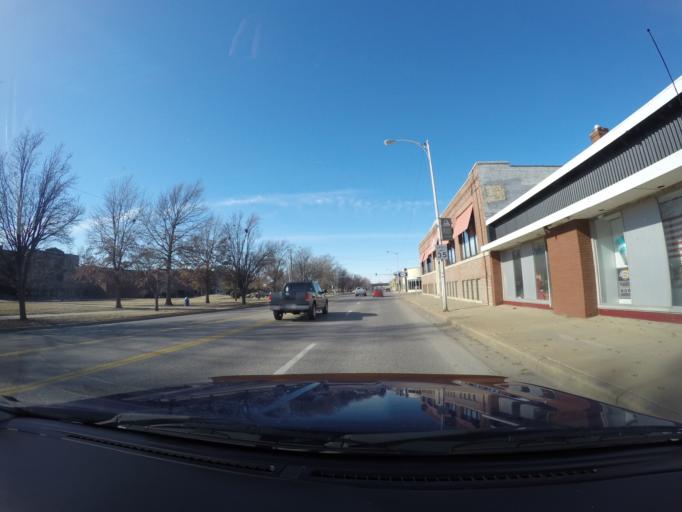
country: US
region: Kansas
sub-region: Sedgwick County
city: Wichita
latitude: 37.6863
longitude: -97.3088
